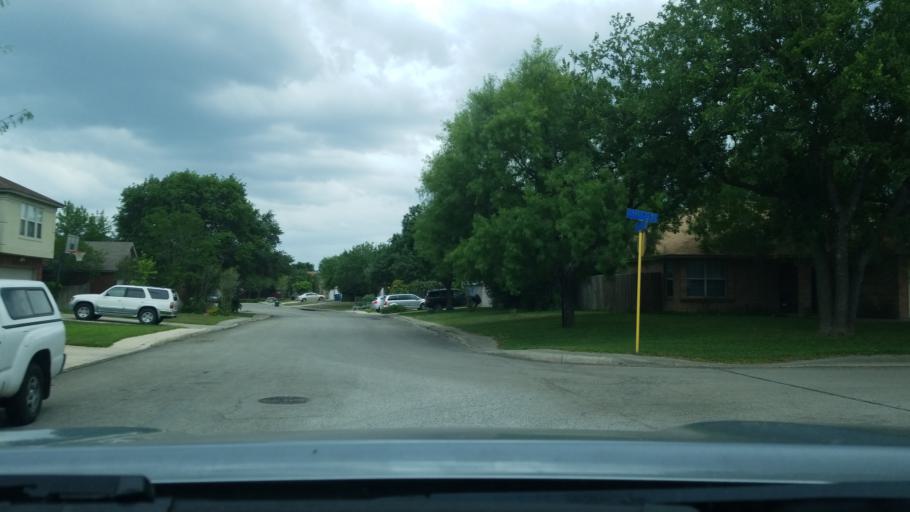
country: US
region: Texas
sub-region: Bexar County
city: Leon Valley
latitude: 29.5405
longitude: -98.6296
